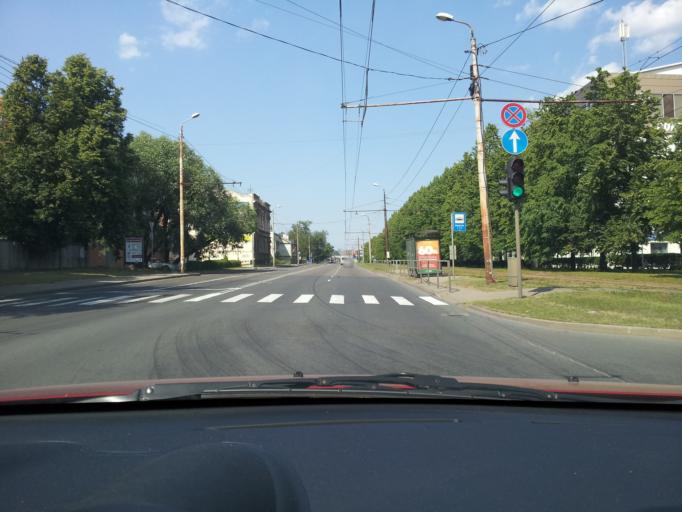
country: LV
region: Riga
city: Riga
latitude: 56.9774
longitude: 24.1140
